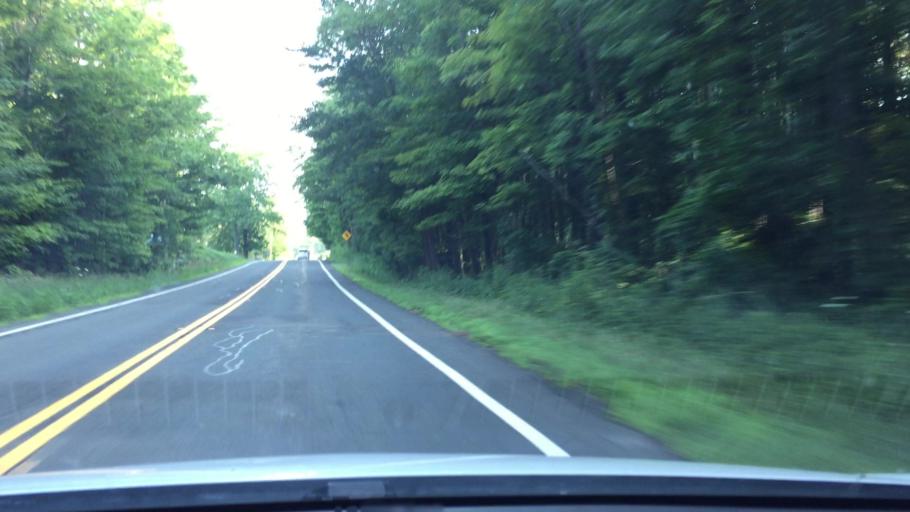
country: US
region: Massachusetts
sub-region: Berkshire County
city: Otis
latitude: 42.2292
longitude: -73.1089
